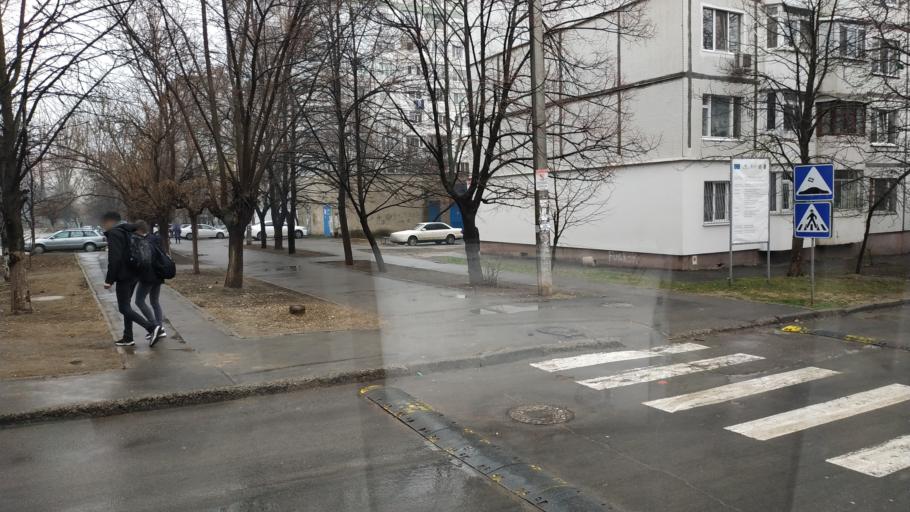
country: MD
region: Chisinau
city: Vatra
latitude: 47.0416
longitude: 28.7677
